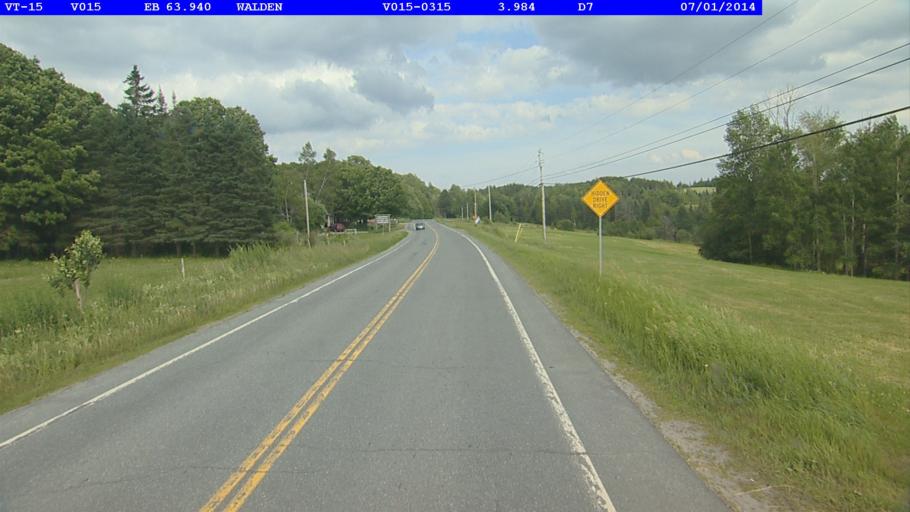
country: US
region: Vermont
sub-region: Caledonia County
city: Hardwick
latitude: 44.4488
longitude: -72.2477
